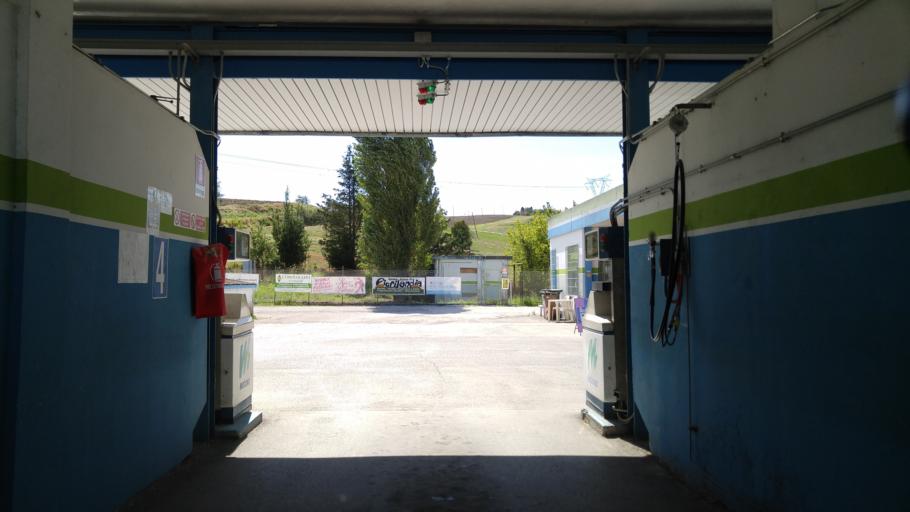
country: IT
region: The Marches
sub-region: Provincia di Pesaro e Urbino
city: Cuccurano
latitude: 43.7938
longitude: 12.9505
